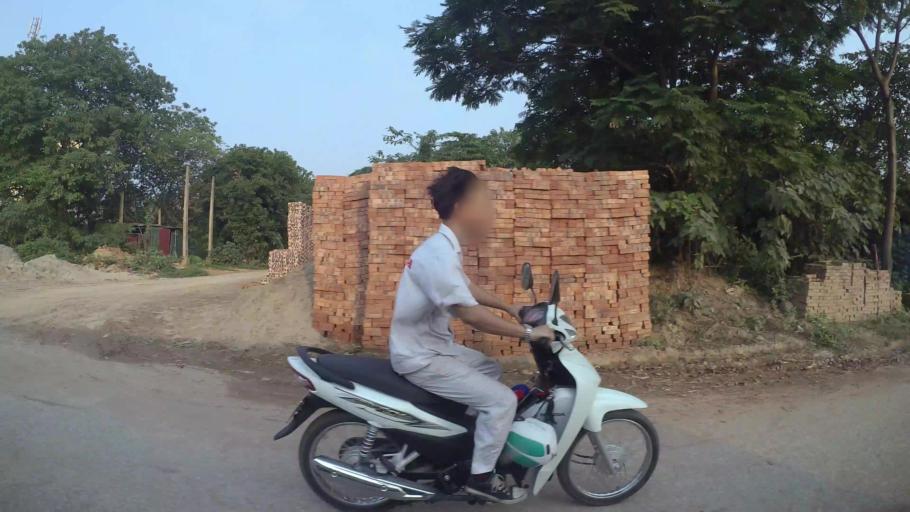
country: VN
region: Ha Noi
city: Tay Ho
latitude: 21.0750
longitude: 105.7953
